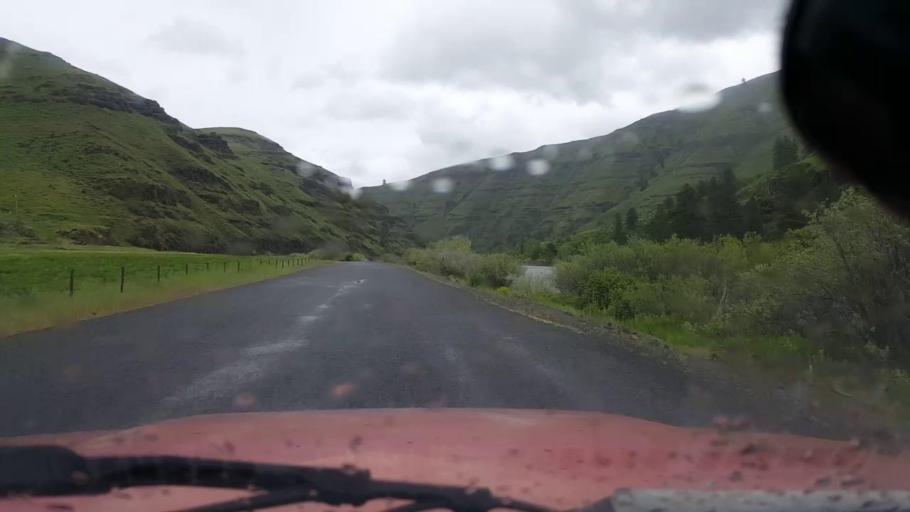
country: US
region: Washington
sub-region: Asotin County
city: Asotin
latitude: 46.0279
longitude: -117.3096
